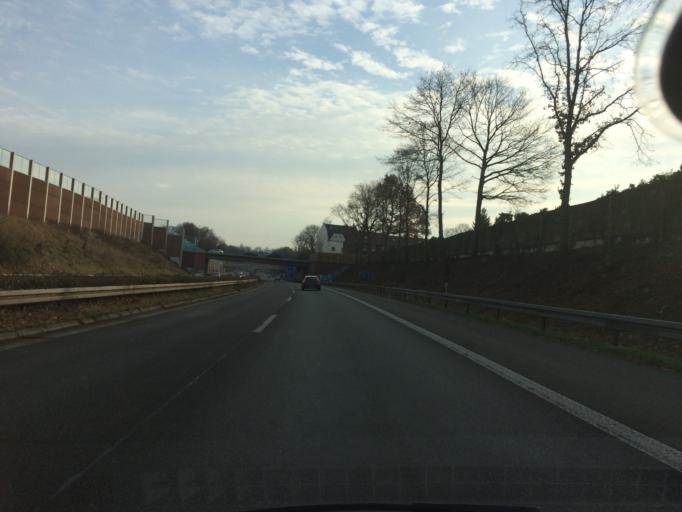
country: DE
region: North Rhine-Westphalia
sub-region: Regierungsbezirk Dusseldorf
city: Oberhausen
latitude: 51.5266
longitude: 6.8482
